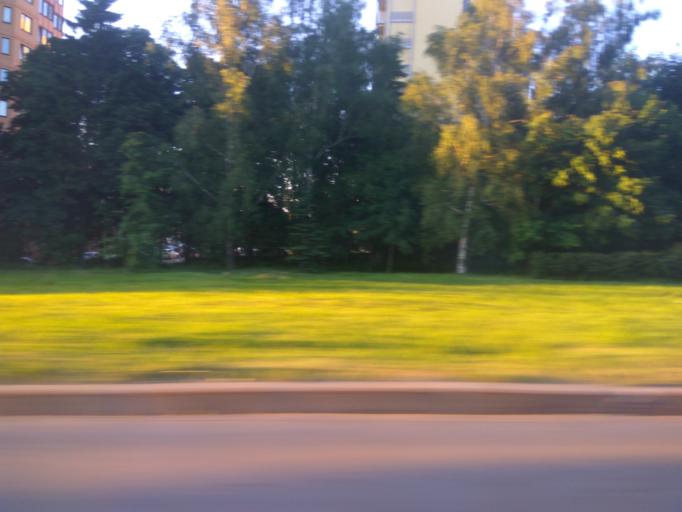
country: RU
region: Moscow
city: Vorob'yovo
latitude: 55.7150
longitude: 37.5215
